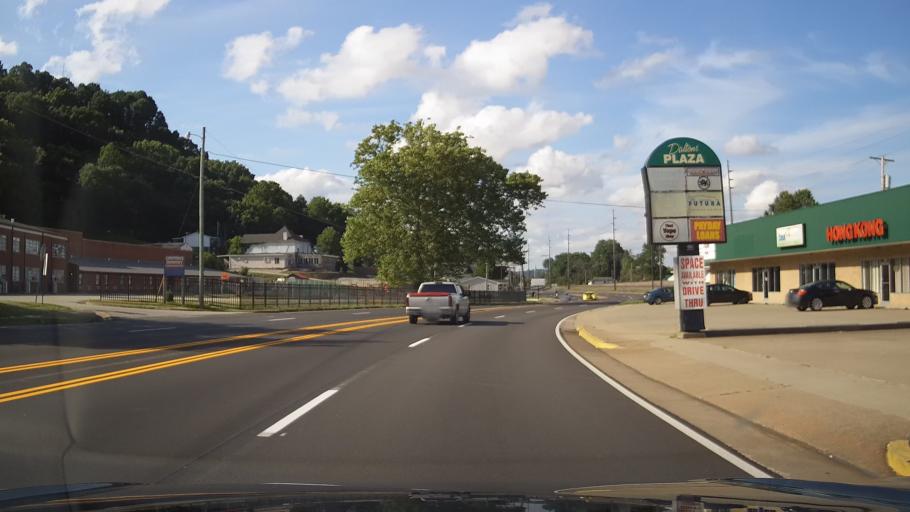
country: US
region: Kentucky
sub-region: Boyd County
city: Catlettsburg
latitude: 38.4062
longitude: -82.6006
